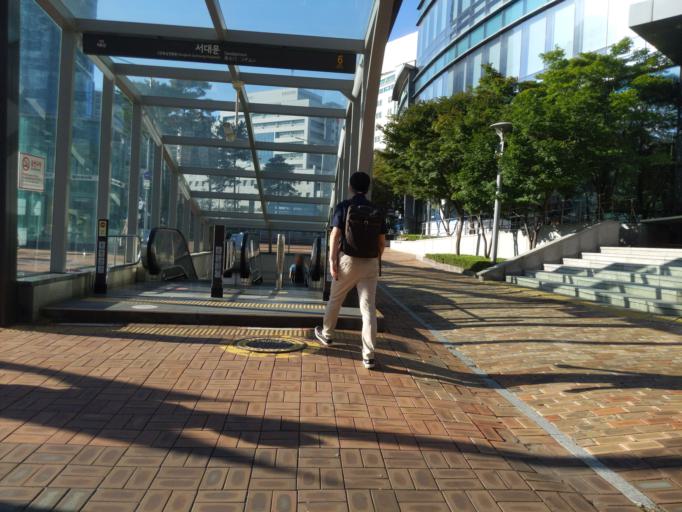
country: KR
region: Seoul
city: Seoul
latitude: 37.5655
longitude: 126.9675
